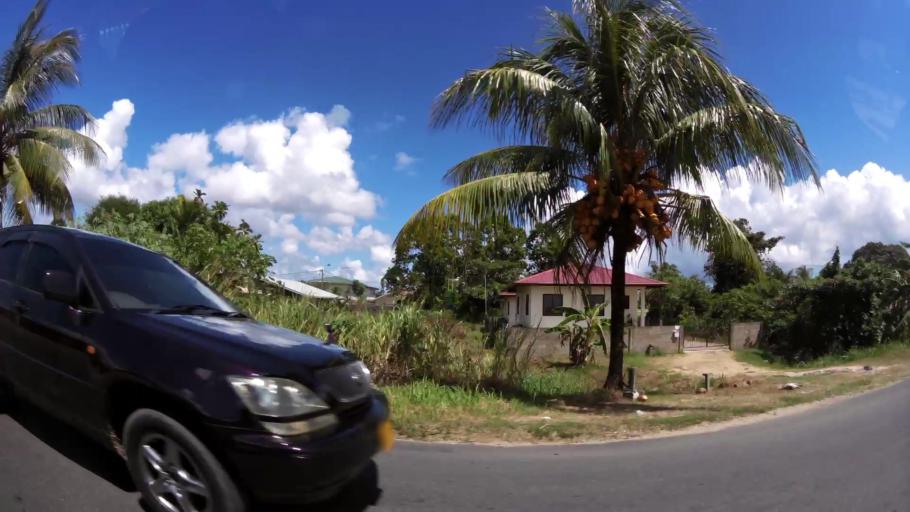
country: SR
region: Paramaribo
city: Paramaribo
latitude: 5.8626
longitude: -55.1270
